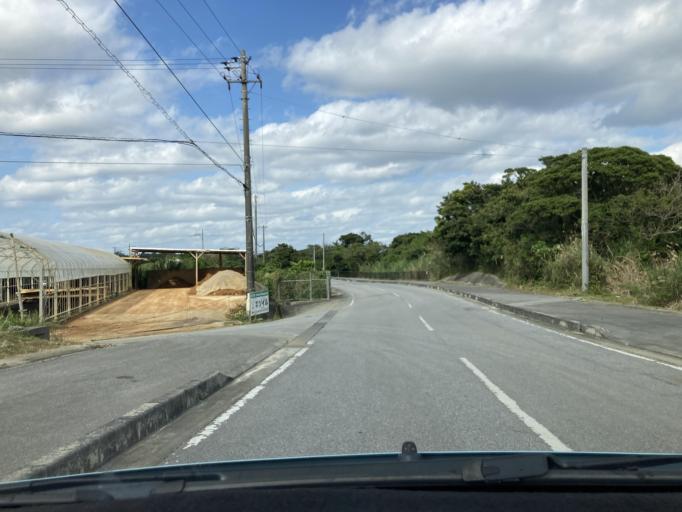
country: JP
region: Okinawa
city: Tomigusuku
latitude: 26.1757
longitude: 127.7611
